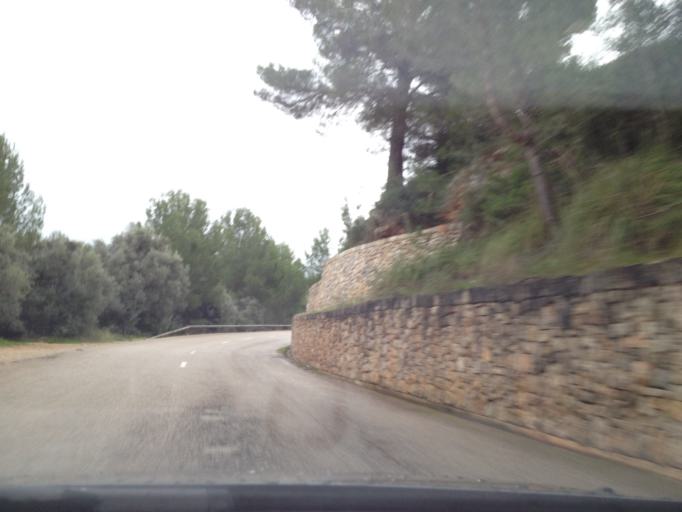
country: ES
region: Balearic Islands
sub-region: Illes Balears
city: Soller
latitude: 39.7750
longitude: 2.6971
